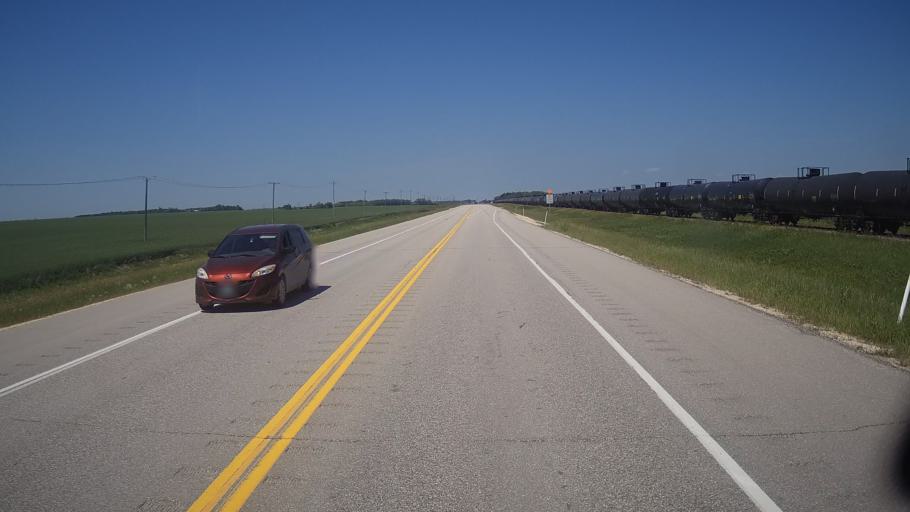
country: CA
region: Manitoba
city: Stonewall
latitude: 50.0980
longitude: -97.4939
